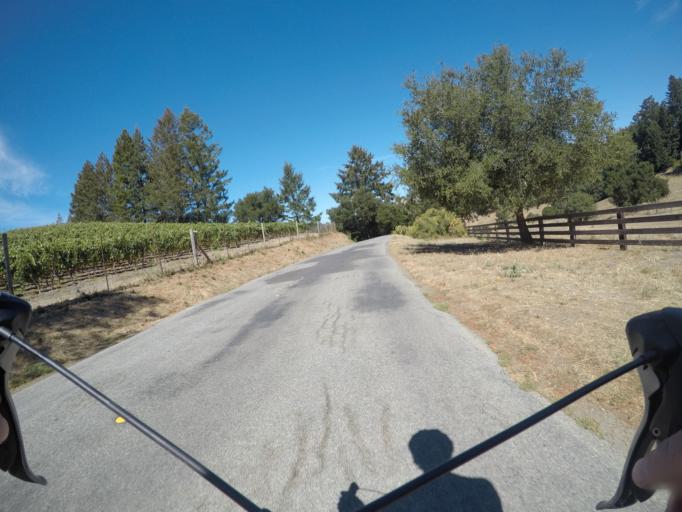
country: US
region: California
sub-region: San Mateo County
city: Portola Valley
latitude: 37.2875
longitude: -122.2183
